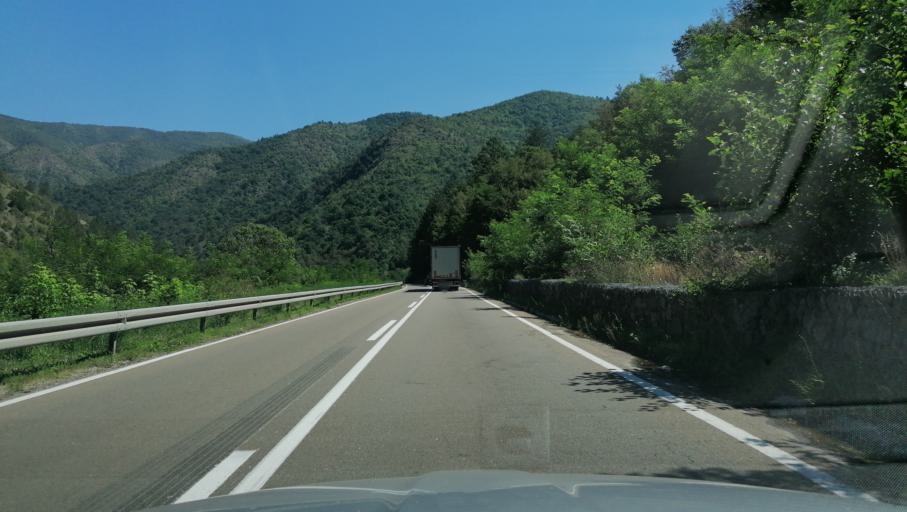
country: RS
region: Central Serbia
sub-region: Raski Okrug
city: Kraljevo
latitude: 43.5498
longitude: 20.6119
